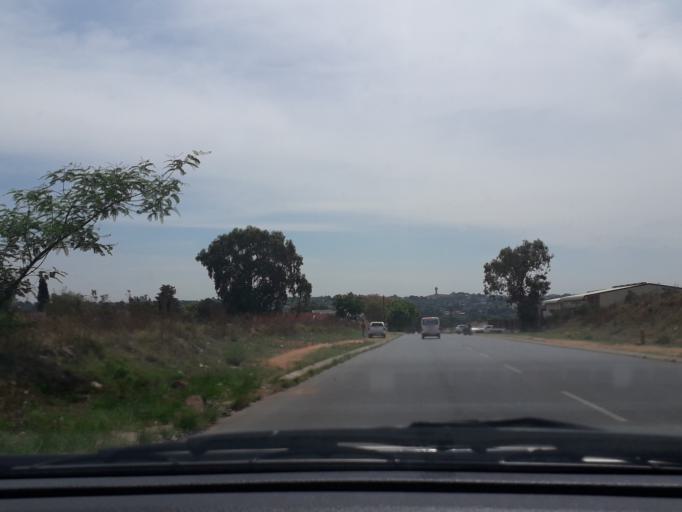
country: ZA
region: Gauteng
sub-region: City of Johannesburg Metropolitan Municipality
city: Roodepoort
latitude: -26.1892
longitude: 27.9247
